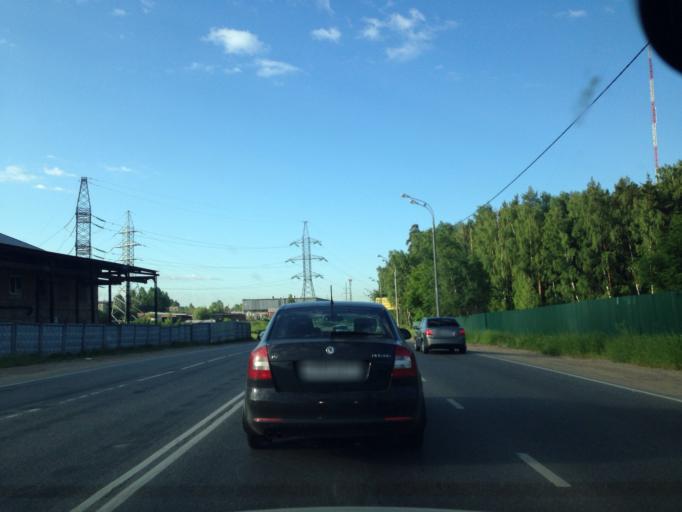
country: RU
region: Moscow
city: Vostochnyy
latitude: 55.7997
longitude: 37.8963
